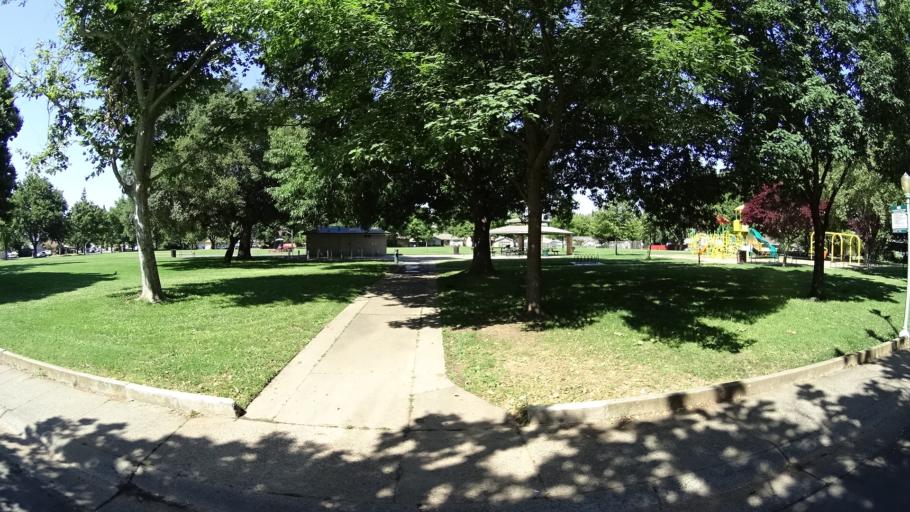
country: US
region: California
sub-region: Sacramento County
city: Parkway
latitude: 38.5288
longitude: -121.4497
